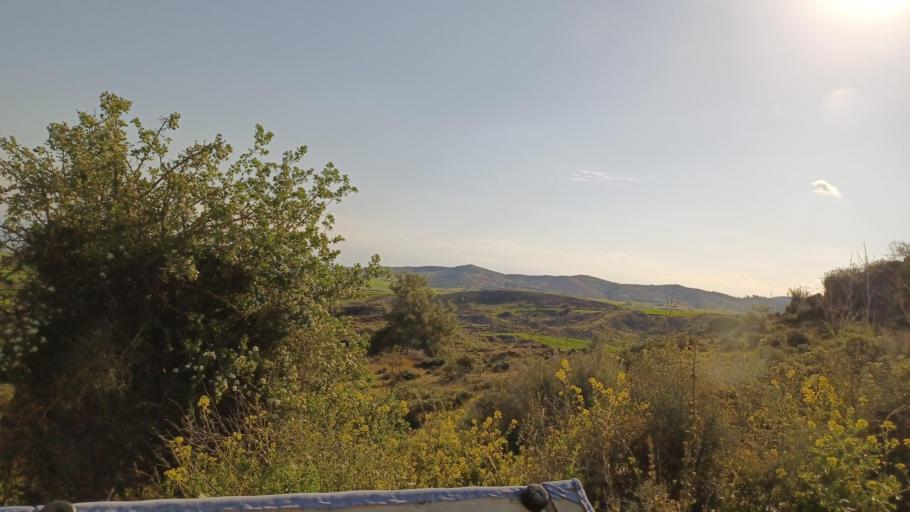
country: CY
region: Lefkosia
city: Lefka
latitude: 35.0788
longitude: 32.9112
